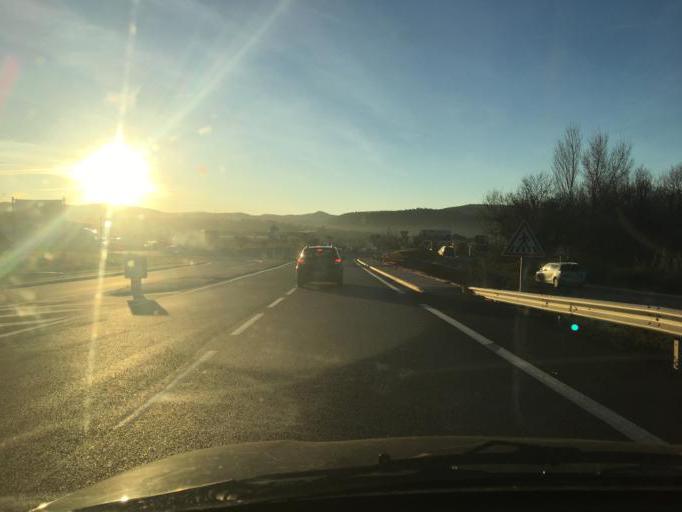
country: FR
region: Provence-Alpes-Cote d'Azur
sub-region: Departement du Var
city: Les Arcs
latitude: 43.4547
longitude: 6.4897
